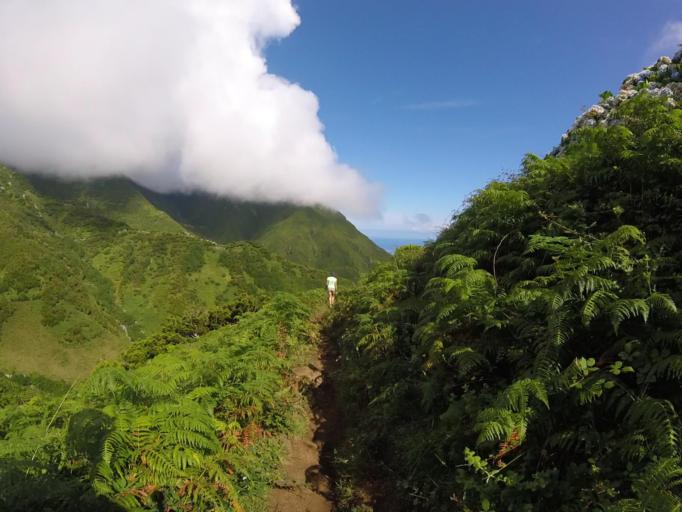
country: PT
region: Azores
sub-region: Sao Roque do Pico
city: Sao Roque do Pico
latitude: 38.6054
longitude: -27.9205
